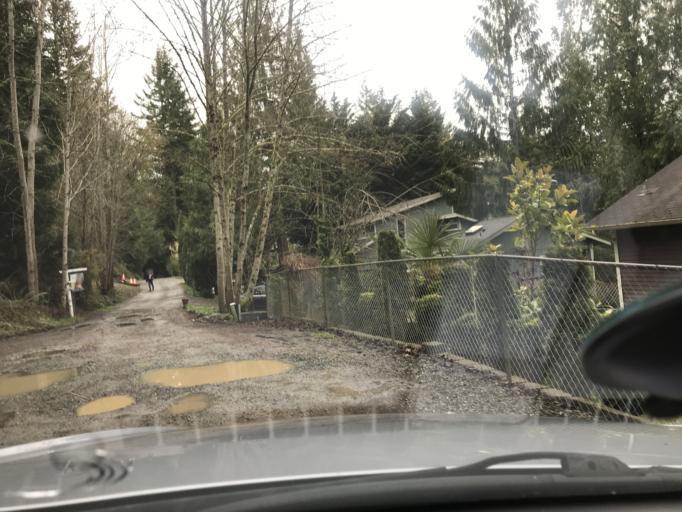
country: US
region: Washington
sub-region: King County
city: Ames Lake
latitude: 47.6407
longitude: -121.9522
